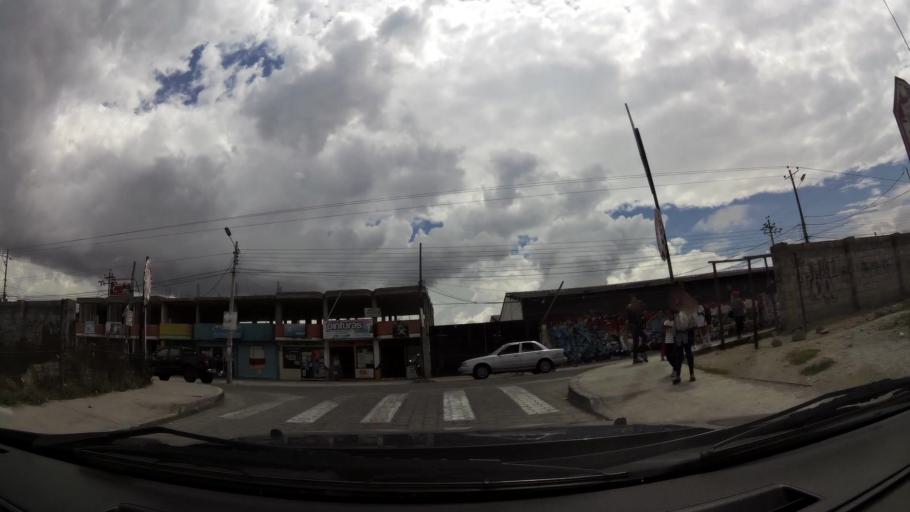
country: EC
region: Pichincha
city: Quito
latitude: -0.0786
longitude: -78.4174
